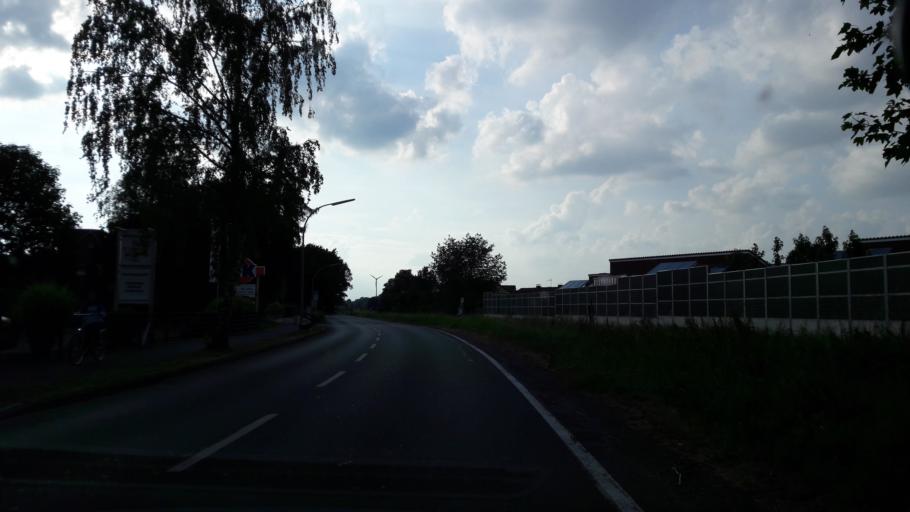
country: DE
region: North Rhine-Westphalia
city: Sendenhorst
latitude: 51.8488
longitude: 7.8241
